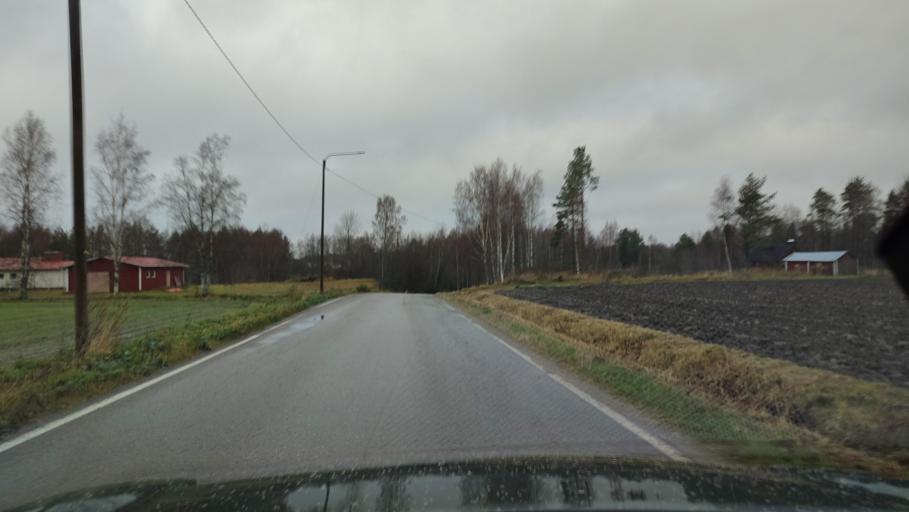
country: FI
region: Southern Ostrobothnia
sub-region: Suupohja
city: Teuva
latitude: 62.4483
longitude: 21.6087
